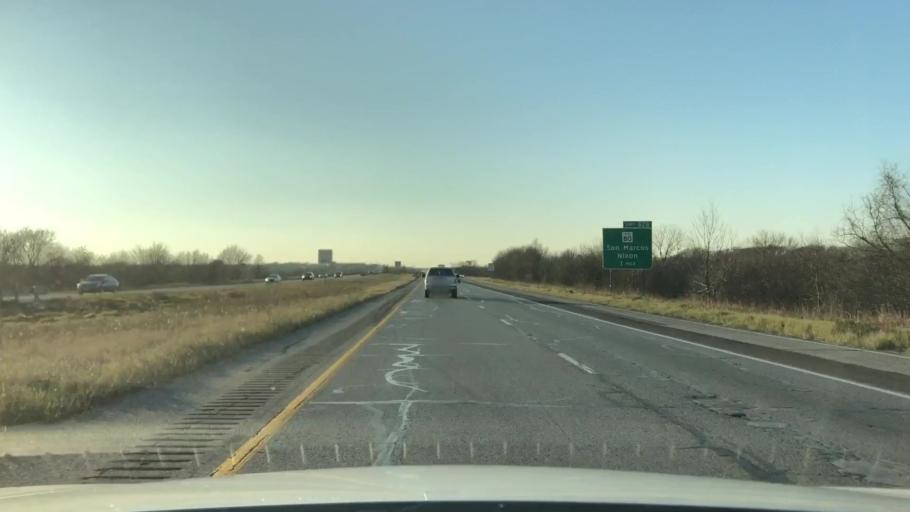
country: US
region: Texas
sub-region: Caldwell County
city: Luling
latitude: 29.6497
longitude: -97.6368
